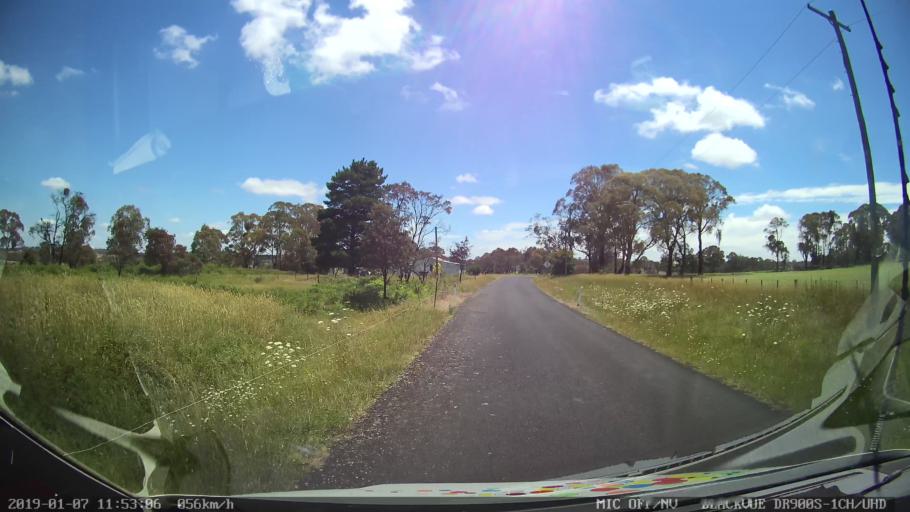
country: AU
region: New South Wales
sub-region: Guyra
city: Guyra
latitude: -30.3070
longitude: 151.6561
